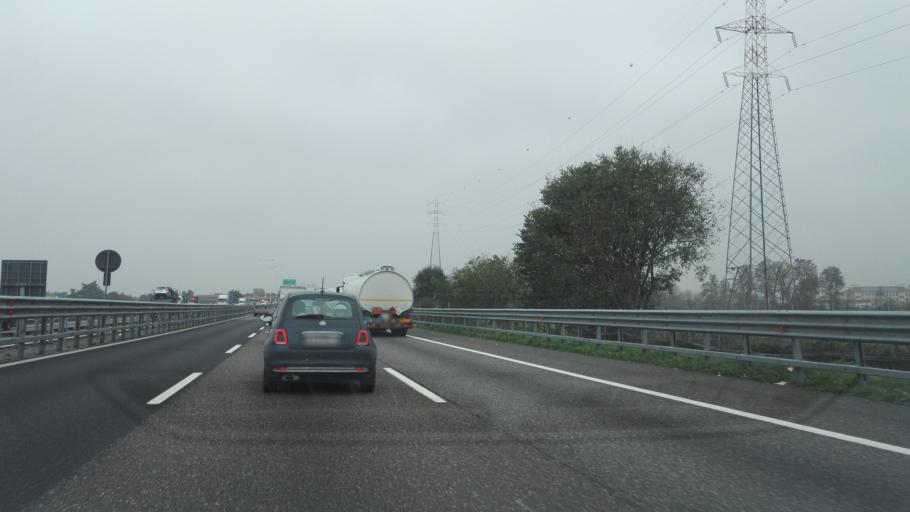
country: IT
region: Lombardy
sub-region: Citta metropolitana di Milano
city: Figino
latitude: 45.4833
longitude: 9.0709
